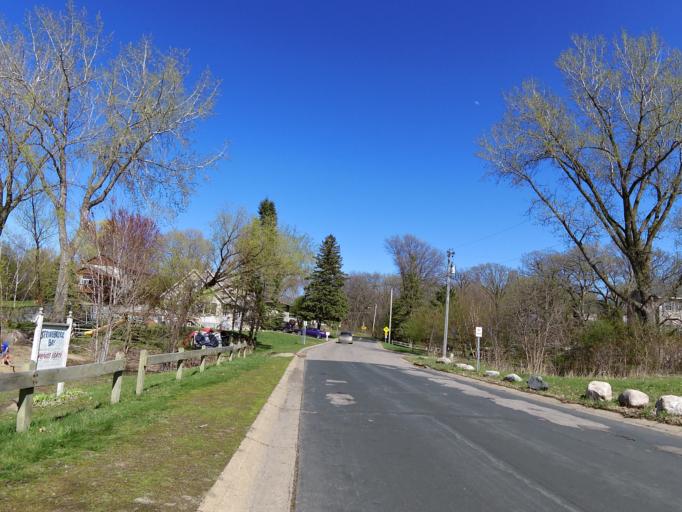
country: US
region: Minnesota
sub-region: Scott County
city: Prior Lake
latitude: 44.7108
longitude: -93.4400
